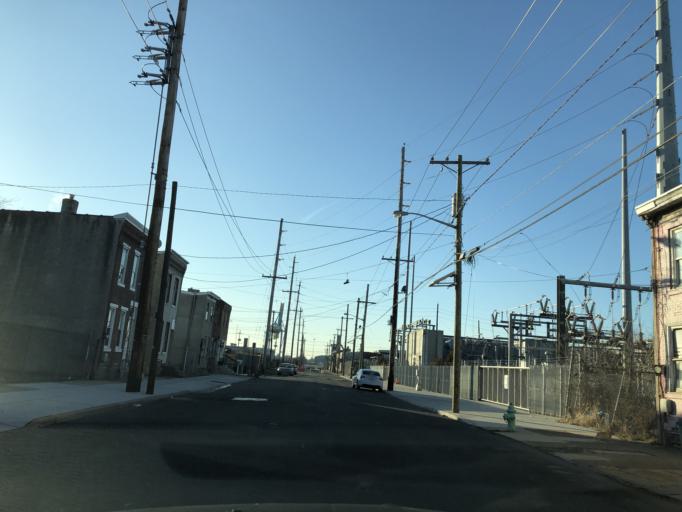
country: US
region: New Jersey
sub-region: Camden County
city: Camden
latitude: 39.9334
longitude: -75.1245
